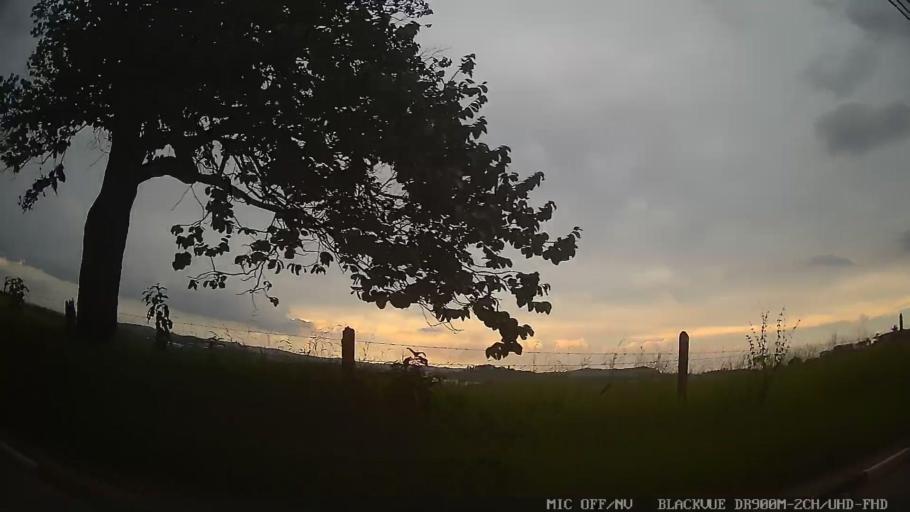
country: BR
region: Sao Paulo
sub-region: Atibaia
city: Atibaia
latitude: -23.1424
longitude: -46.5908
